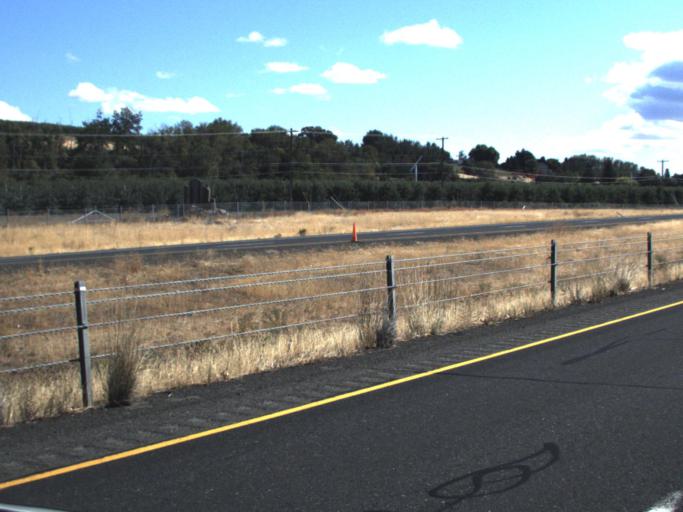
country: US
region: Washington
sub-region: Yakima County
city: Gleed
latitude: 46.6809
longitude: -120.6489
